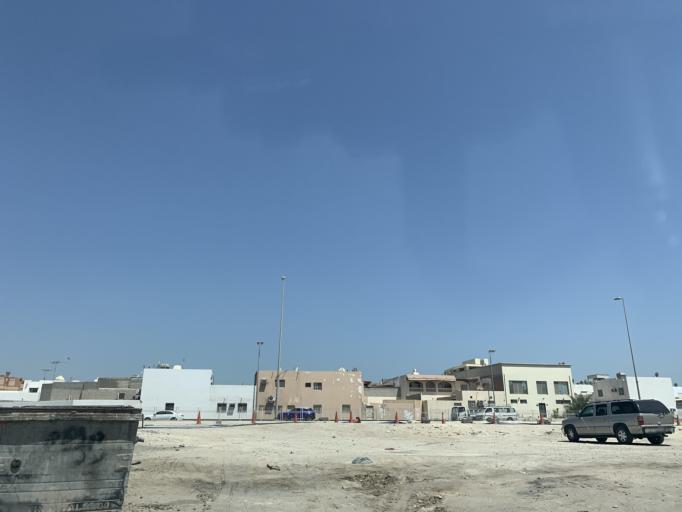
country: BH
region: Northern
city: Ar Rifa'
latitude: 26.1374
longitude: 50.5738
